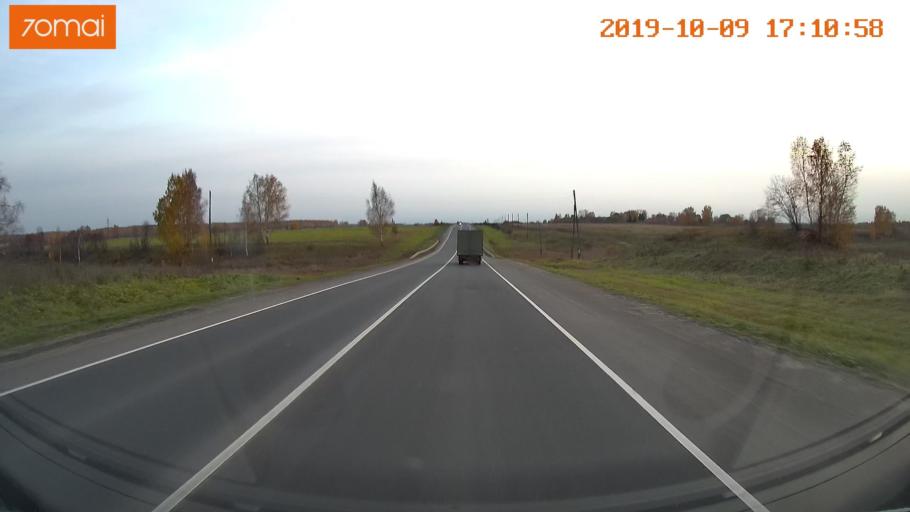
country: RU
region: Ivanovo
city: Privolzhsk
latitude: 57.3487
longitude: 41.2534
